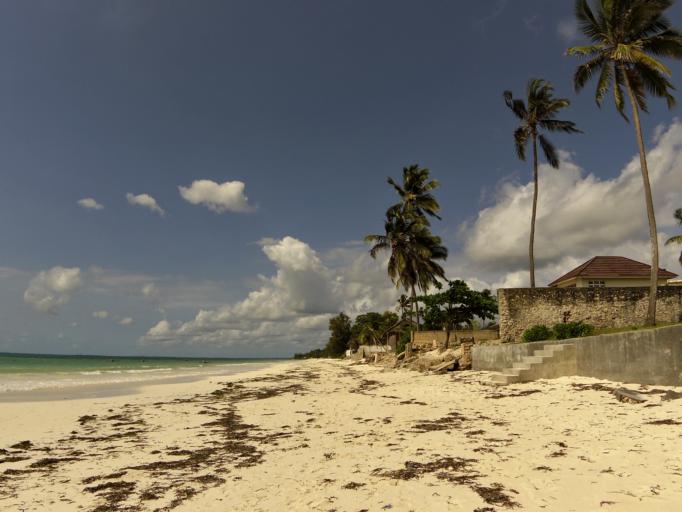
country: TZ
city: Kiwengwa
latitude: -6.1007
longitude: 39.4263
